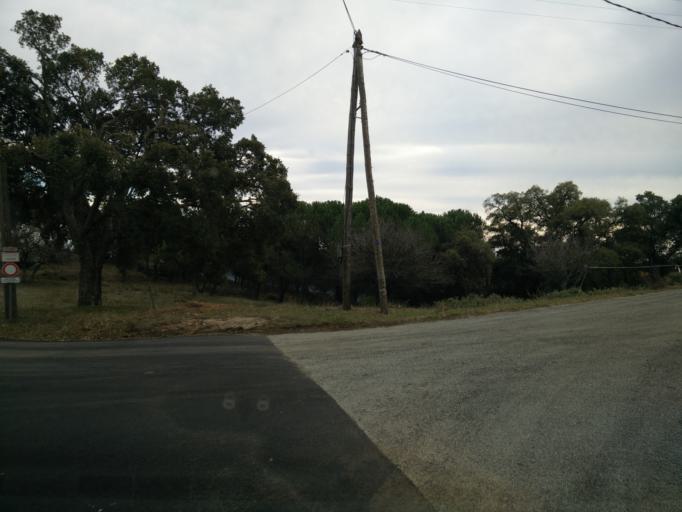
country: FR
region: Provence-Alpes-Cote d'Azur
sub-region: Departement du Var
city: Sainte-Maxime
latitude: 43.3661
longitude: 6.6176
